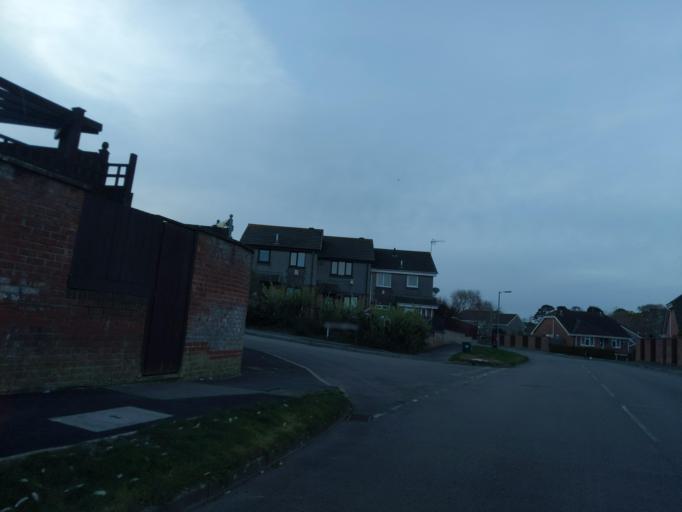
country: GB
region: England
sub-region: Cornwall
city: Torpoint
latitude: 50.3780
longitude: -4.2132
